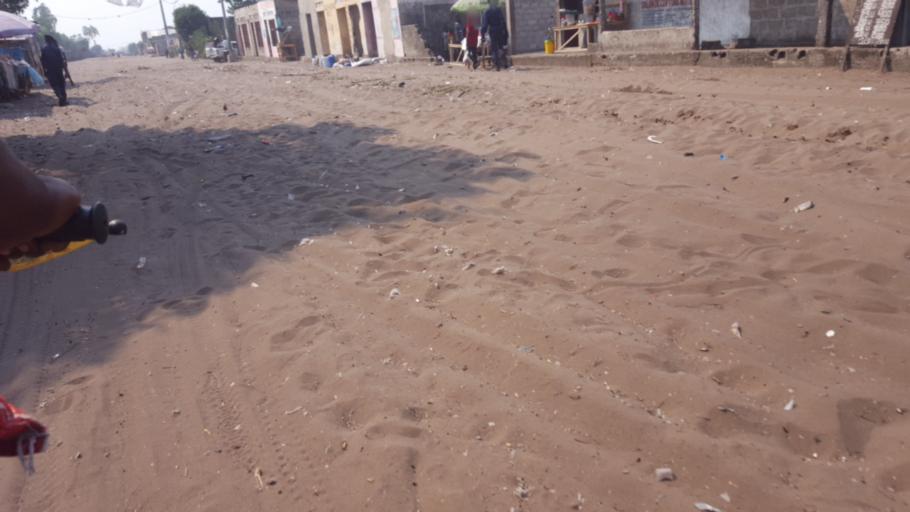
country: CD
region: Kinshasa
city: Masina
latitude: -4.3615
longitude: 15.5086
